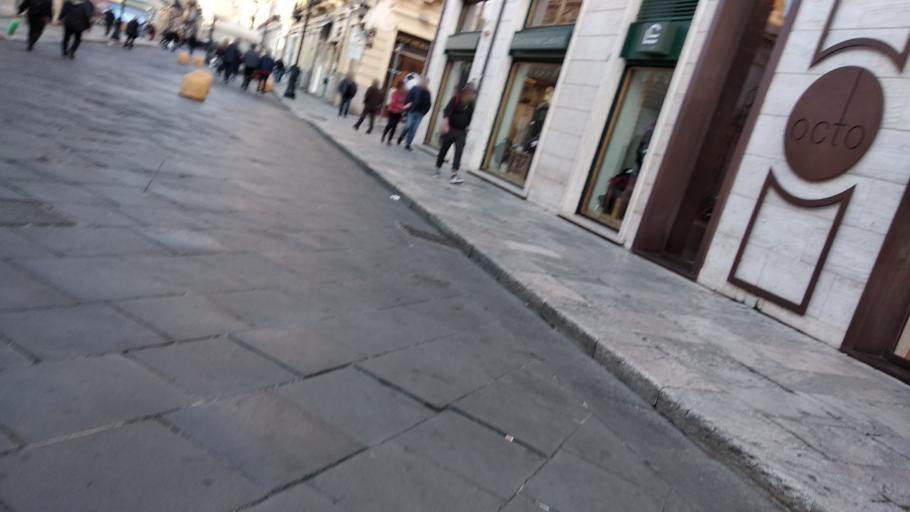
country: IT
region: Calabria
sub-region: Provincia di Reggio Calabria
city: Reggio Calabria
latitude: 38.1093
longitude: 15.6452
